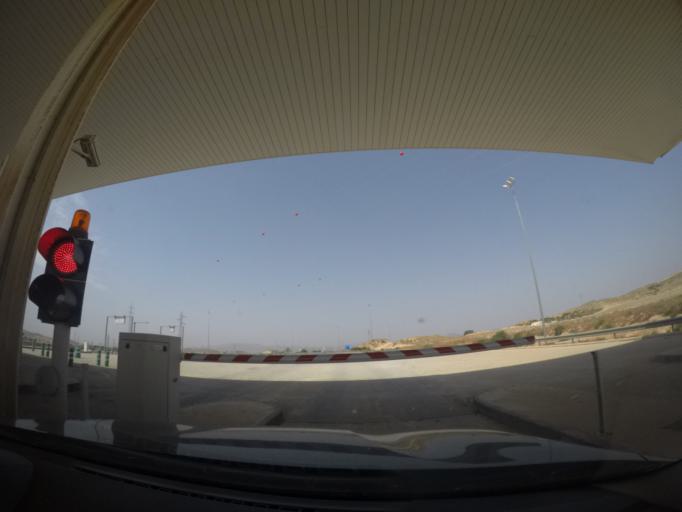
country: ES
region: Andalusia
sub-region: Provincia de Almeria
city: Vera
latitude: 37.2618
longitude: -1.8806
